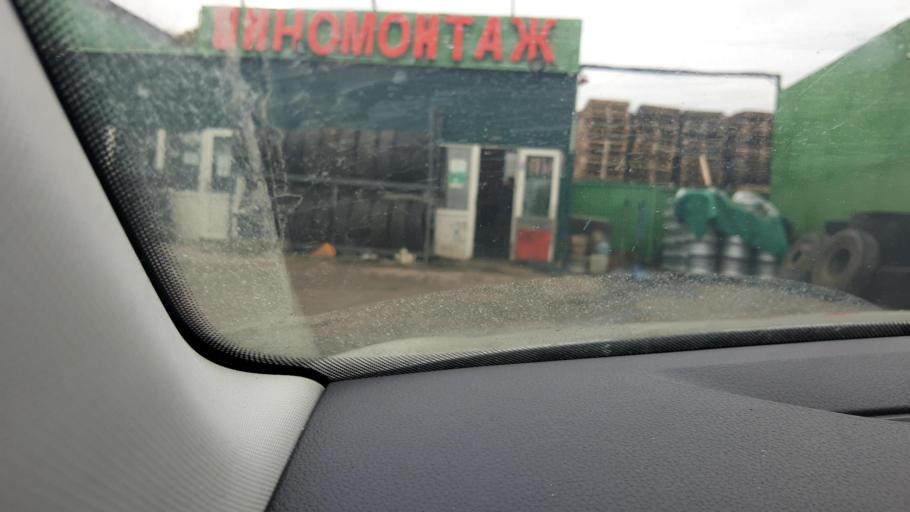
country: RU
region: Moscow
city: Annino
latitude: 55.5740
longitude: 37.6192
